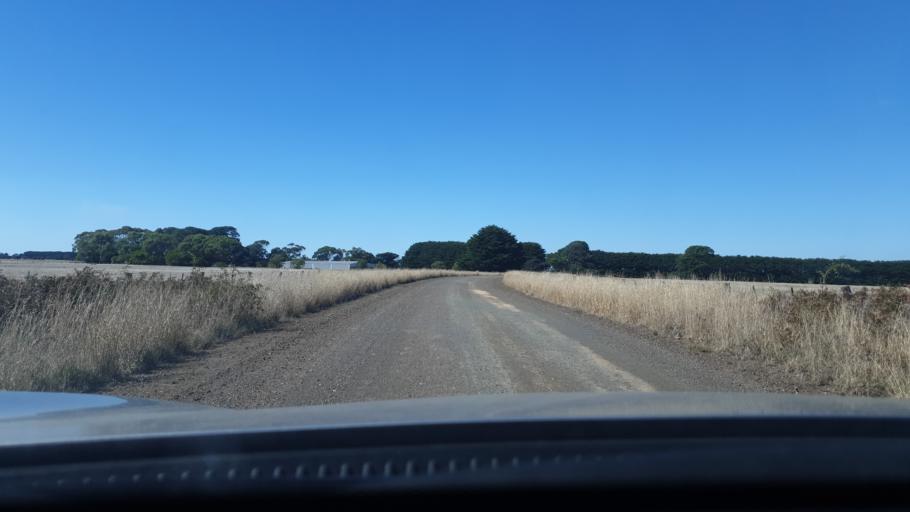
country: AU
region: Victoria
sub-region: Warrnambool
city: Warrnambool
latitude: -38.1653
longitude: 142.3717
